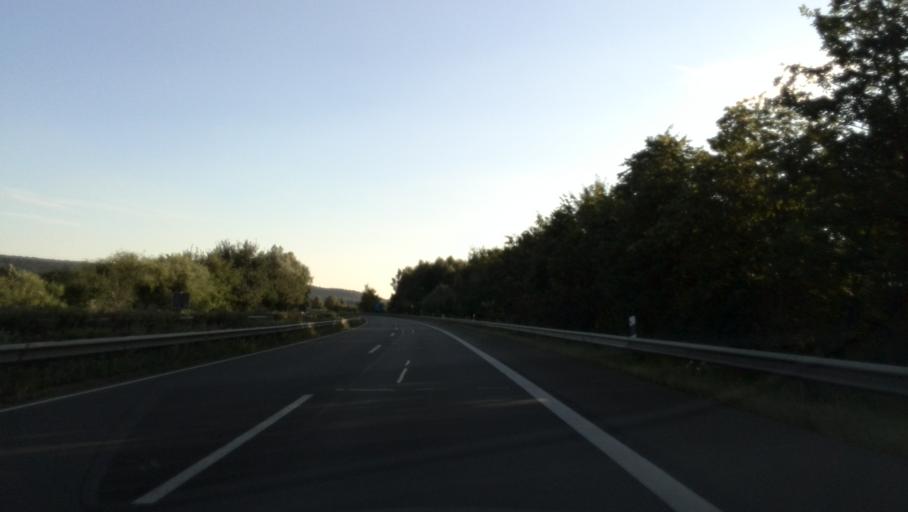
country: DE
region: Lower Saxony
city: Burgdorf
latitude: 52.1336
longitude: 10.2425
